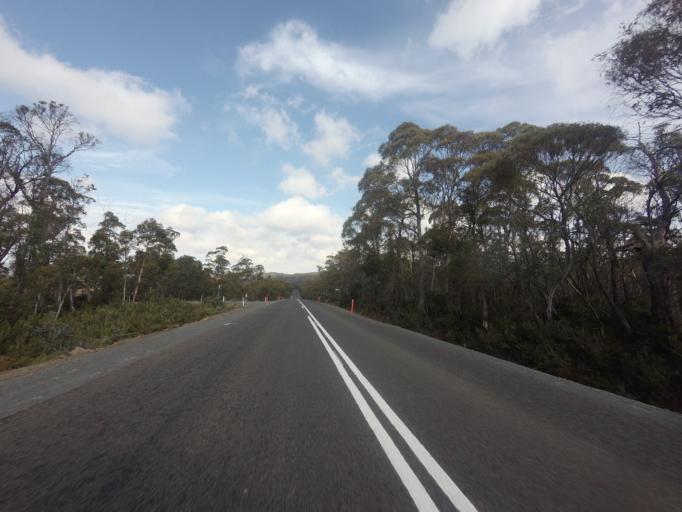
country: AU
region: Tasmania
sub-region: Meander Valley
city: Deloraine
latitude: -41.8328
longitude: 146.6781
